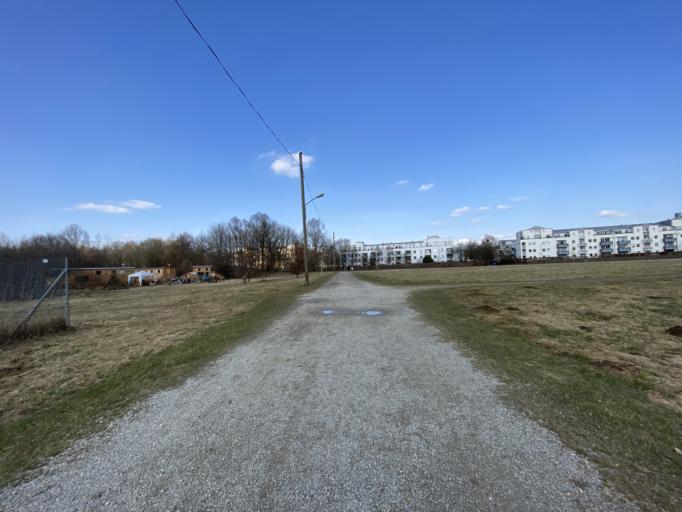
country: DE
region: Bavaria
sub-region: Upper Bavaria
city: Unterfoehring
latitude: 48.1646
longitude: 11.6412
